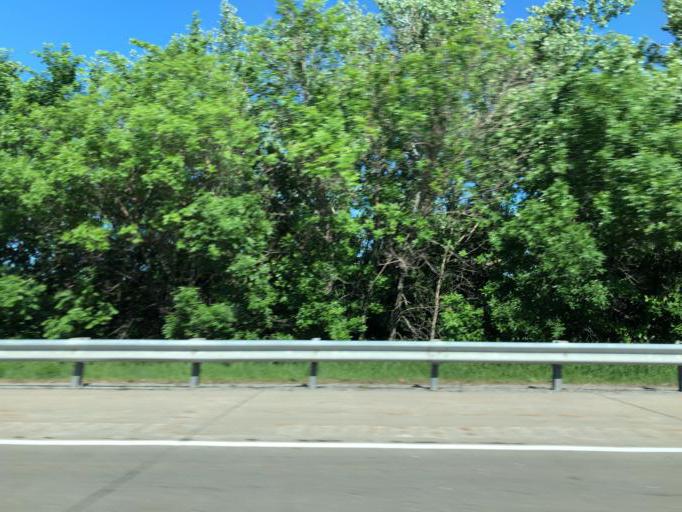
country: US
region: Nebraska
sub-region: Saunders County
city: Ashland
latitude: 41.0203
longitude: -96.3028
